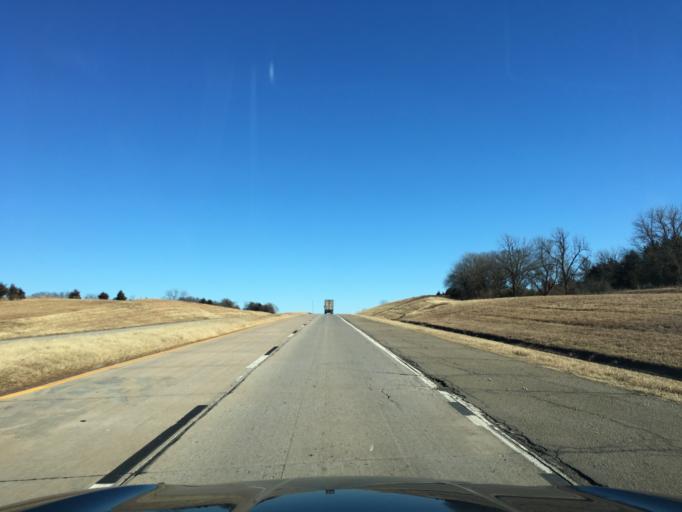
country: US
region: Oklahoma
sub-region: Pawnee County
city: Pawnee
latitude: 36.2248
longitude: -96.7760
